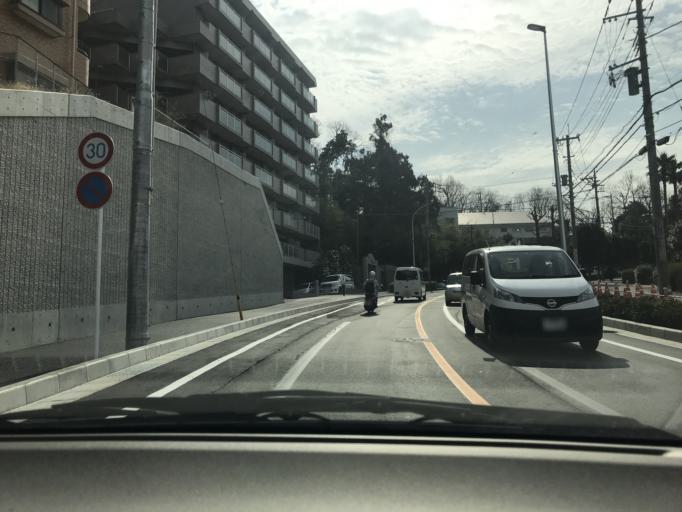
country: JP
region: Tokyo
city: Chofugaoka
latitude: 35.6089
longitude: 139.5518
